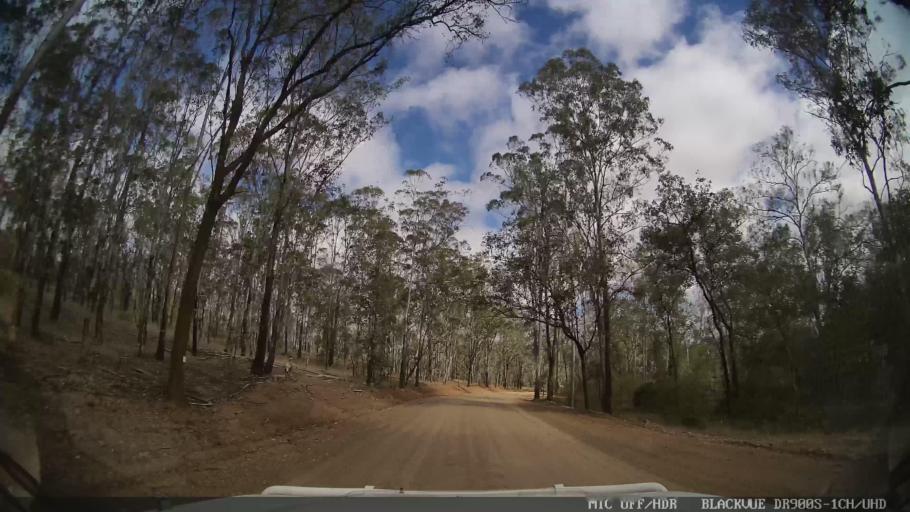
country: AU
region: Queensland
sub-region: Gladstone
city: Toolooa
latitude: -24.6850
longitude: 151.3284
